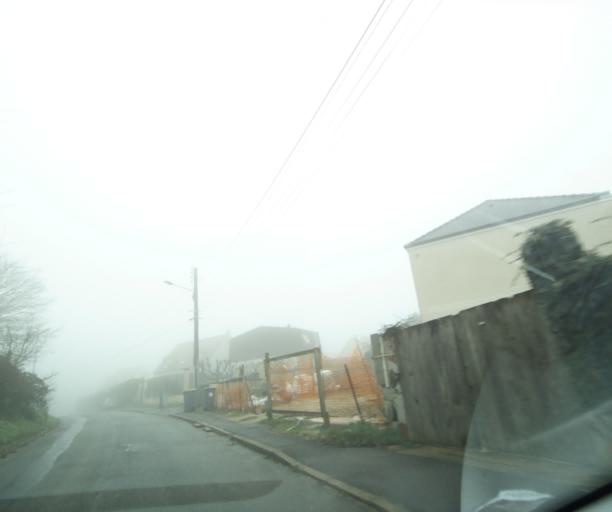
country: FR
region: Ile-de-France
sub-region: Departement de Seine-et-Marne
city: Dammartin-en-Goele
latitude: 49.0519
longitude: 2.6904
